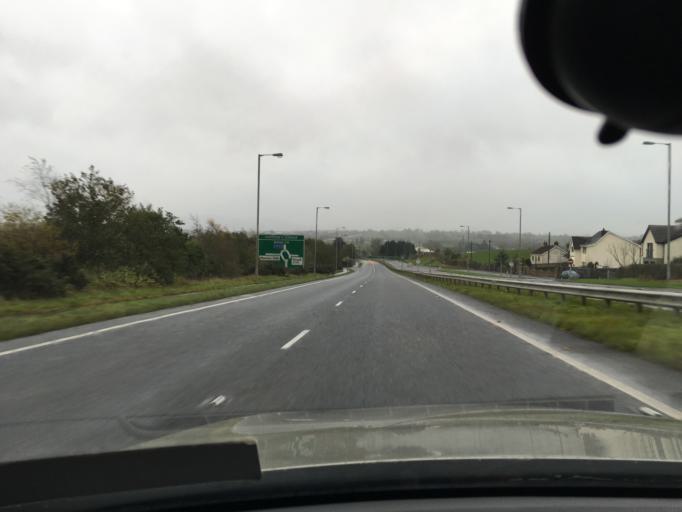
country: GB
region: Northern Ireland
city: Carnmoney
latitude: 54.7085
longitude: -5.9680
